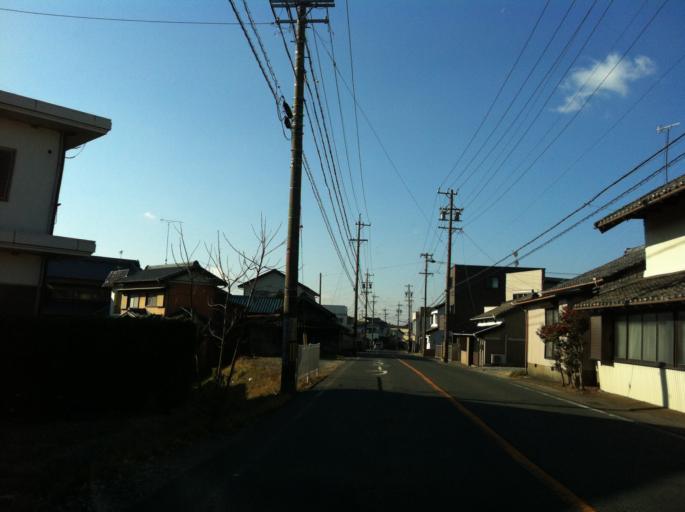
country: JP
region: Aichi
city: Tahara
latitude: 34.6945
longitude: 137.3376
